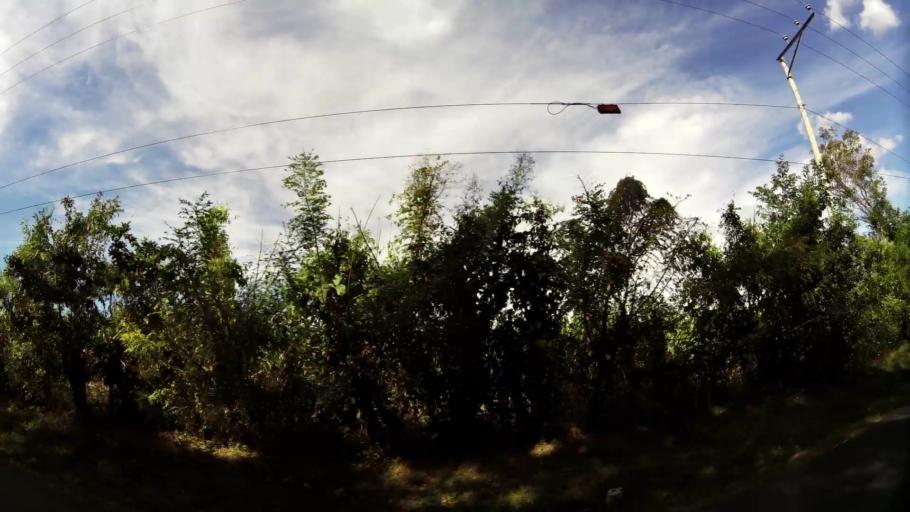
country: SV
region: San Salvador
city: Aguilares
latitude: 13.9581
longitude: -89.1490
